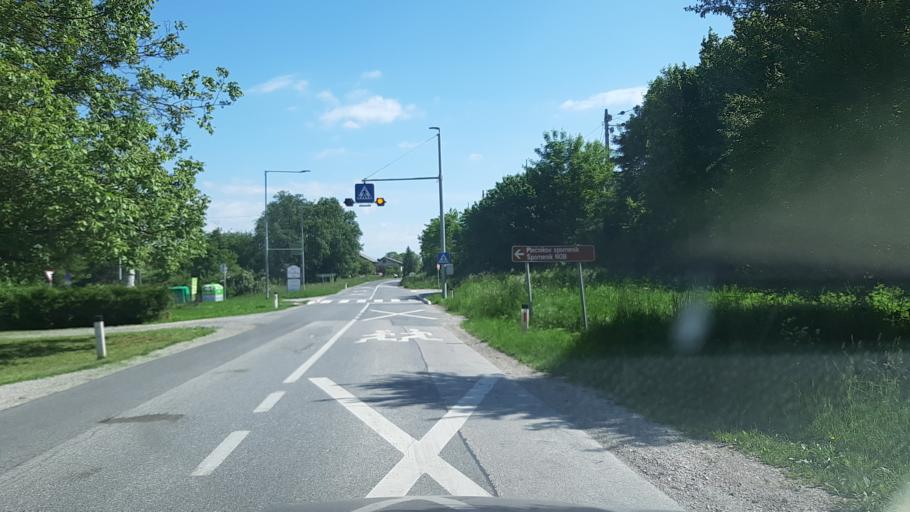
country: SI
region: Borovnica
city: Borovnica
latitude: 45.9367
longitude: 14.3635
